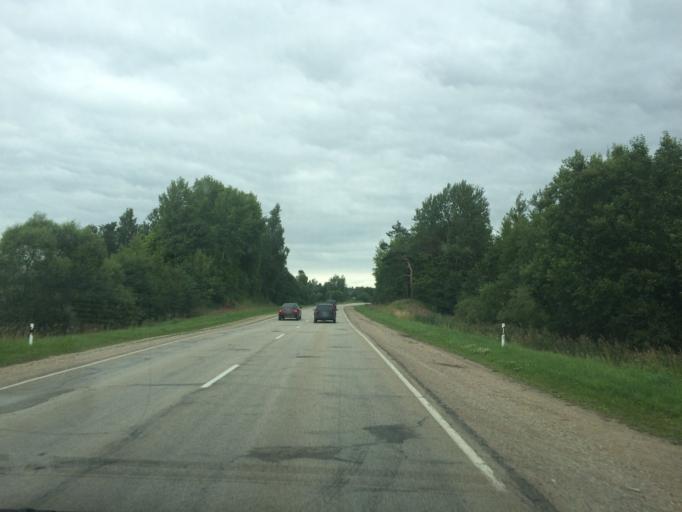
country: LV
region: Rezekne
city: Rezekne
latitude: 56.5661
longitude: 27.3674
